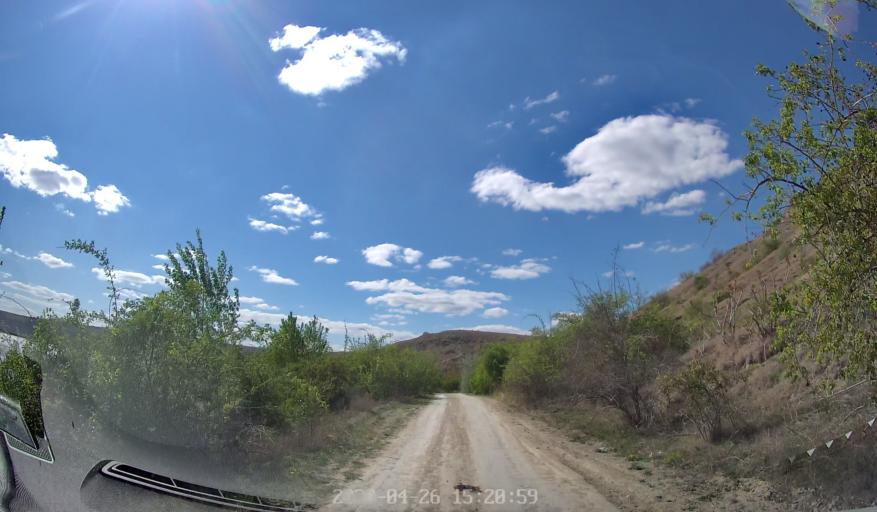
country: MD
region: Telenesti
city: Cocieri
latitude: 47.3642
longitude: 29.0948
